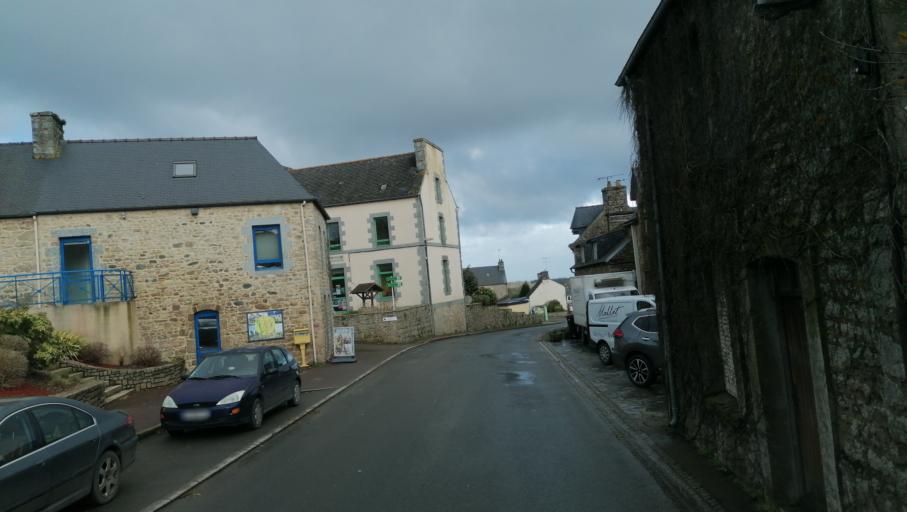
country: FR
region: Brittany
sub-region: Departement des Cotes-d'Armor
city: Lanrodec
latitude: 48.5172
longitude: -3.0310
